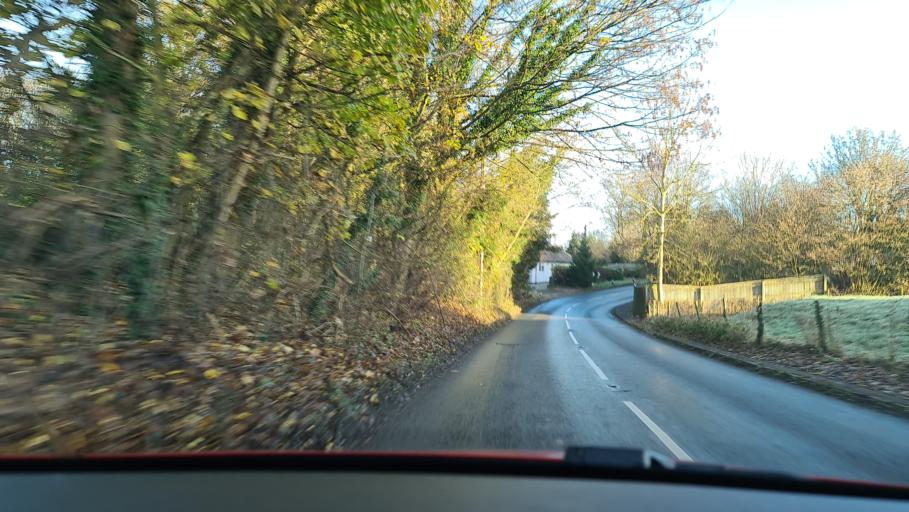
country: GB
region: England
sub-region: Buckinghamshire
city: Princes Risborough
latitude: 51.7506
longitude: -0.8044
